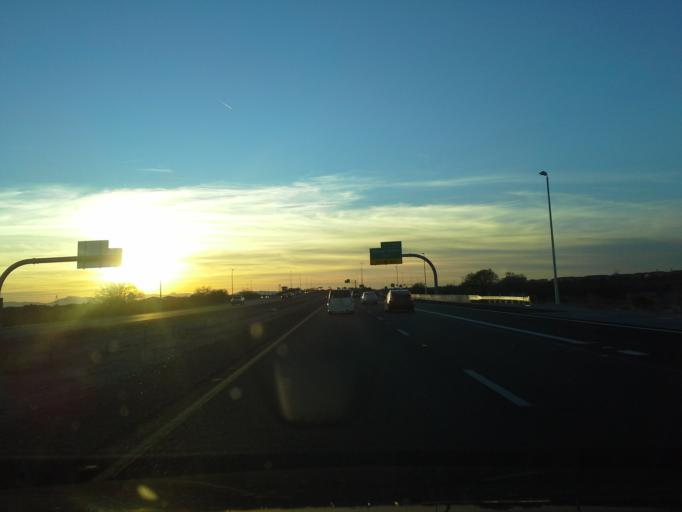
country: US
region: Arizona
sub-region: Pinal County
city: Apache Junction
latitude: 33.3867
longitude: -111.5903
